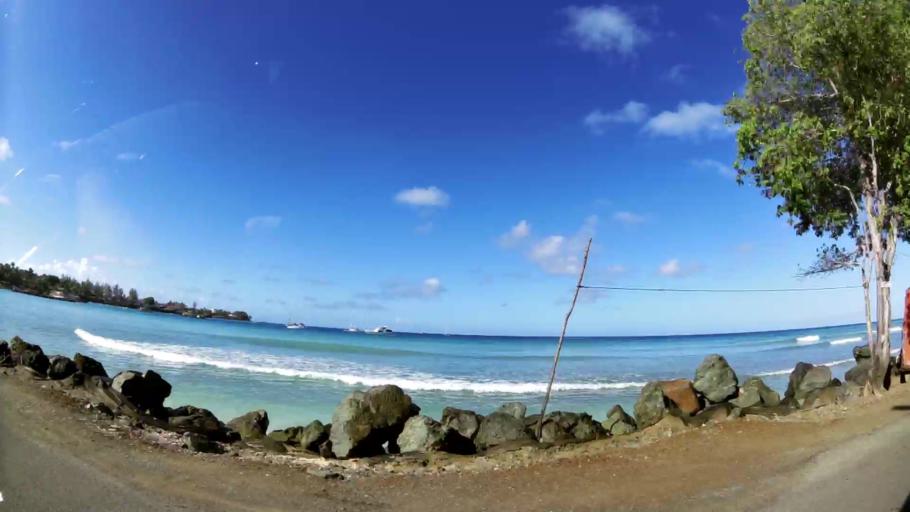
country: TT
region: Tobago
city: Scarborough
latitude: 11.1602
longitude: -60.8390
